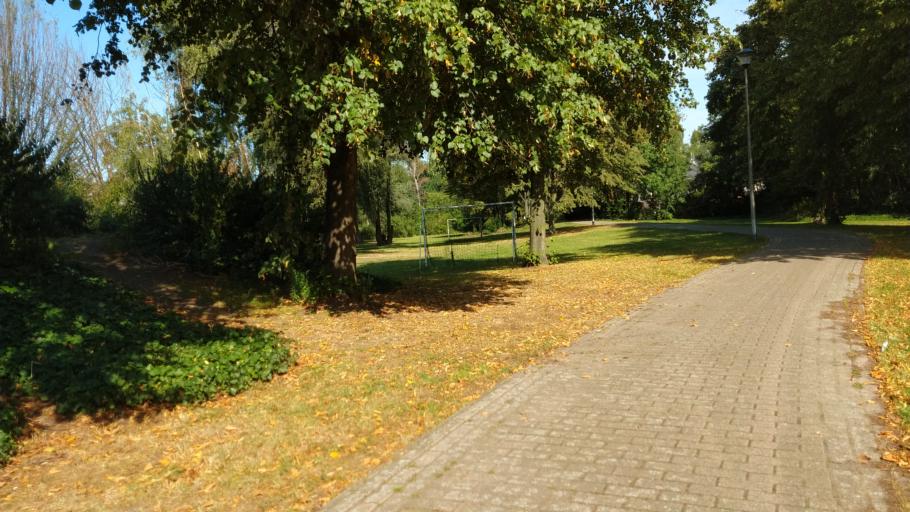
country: BE
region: Flanders
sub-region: Provincie Oost-Vlaanderen
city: Zelzate
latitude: 51.1993
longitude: 3.8056
